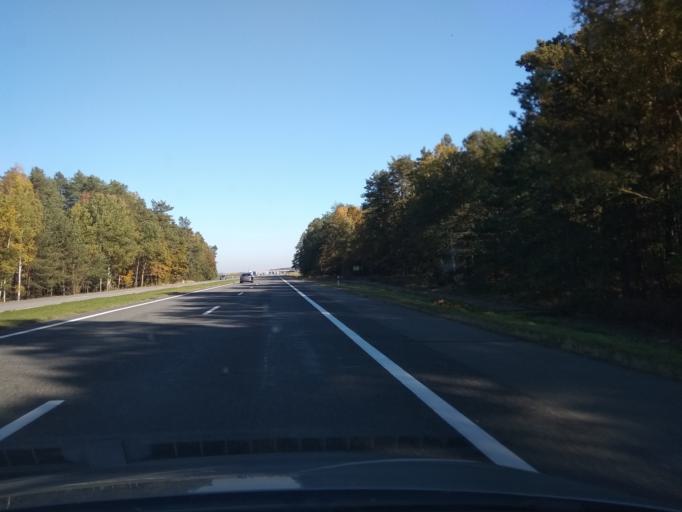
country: BY
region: Brest
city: Antopal'
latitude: 52.3815
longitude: 24.7616
